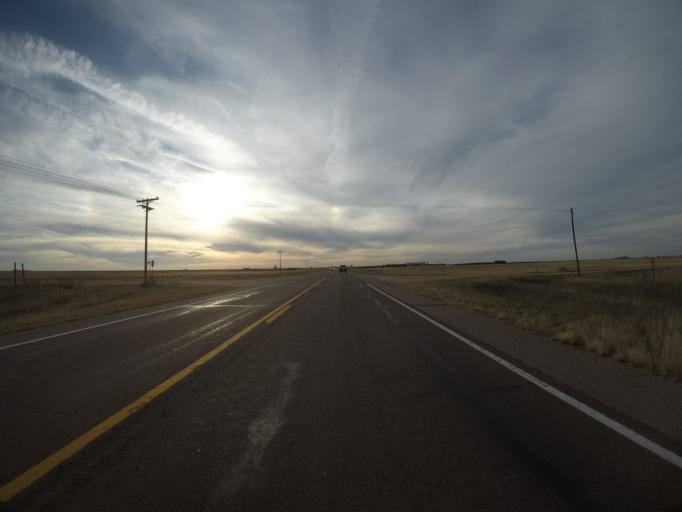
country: US
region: Colorado
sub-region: Yuma County
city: Yuma
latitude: 39.6561
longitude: -102.6303
